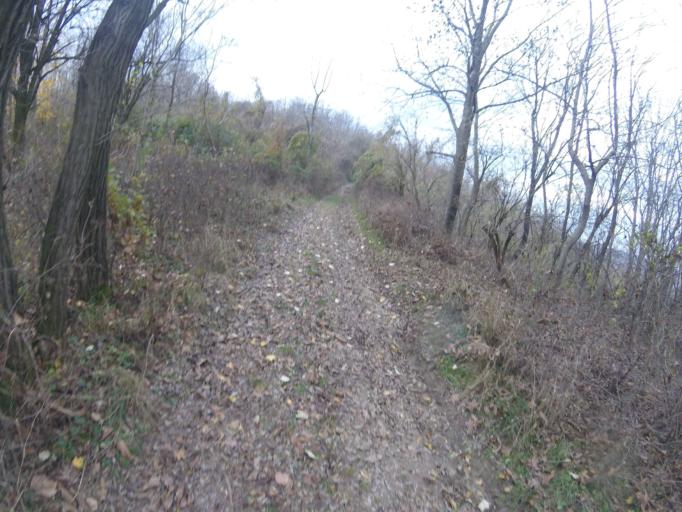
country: HU
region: Tolna
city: Szekszard
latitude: 46.3233
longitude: 18.6593
